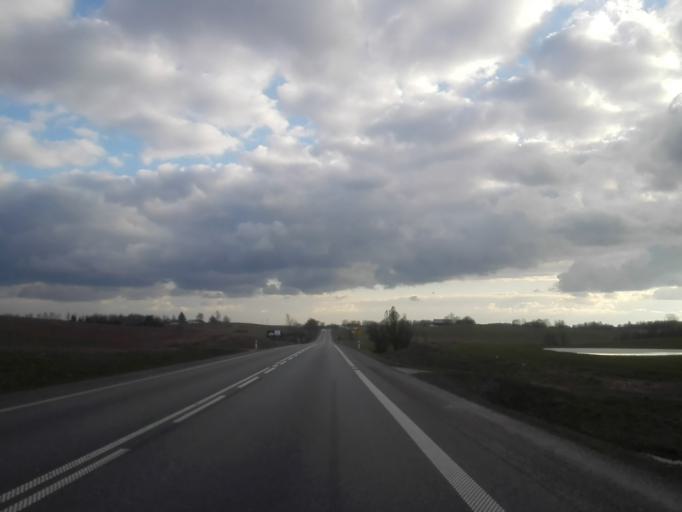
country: PL
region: Podlasie
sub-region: Suwalki
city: Suwalki
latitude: 54.2077
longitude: 23.0255
